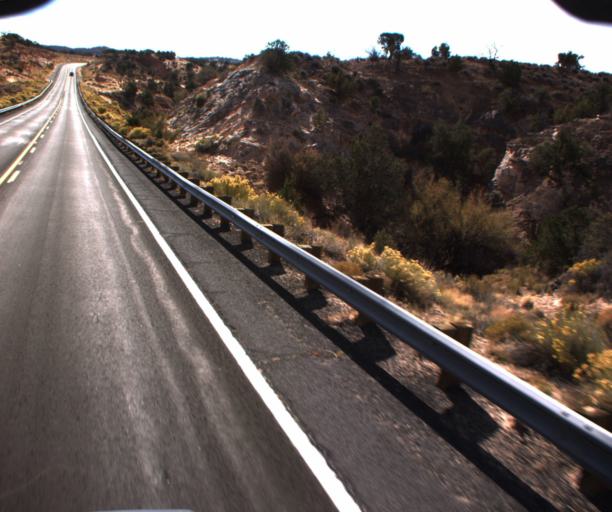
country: US
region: Arizona
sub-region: Coconino County
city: Kaibito
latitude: 36.6036
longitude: -110.9188
